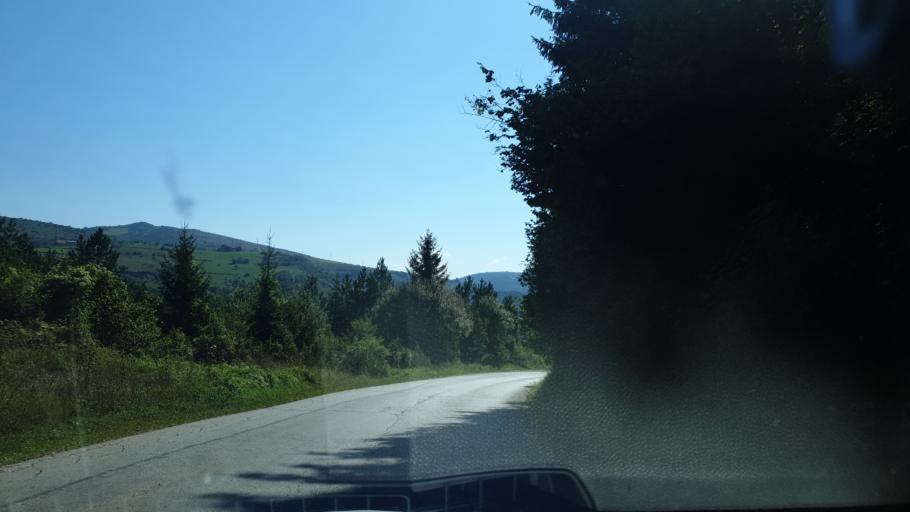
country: RS
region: Central Serbia
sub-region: Zlatiborski Okrug
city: Nova Varos
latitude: 43.4230
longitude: 19.9225
